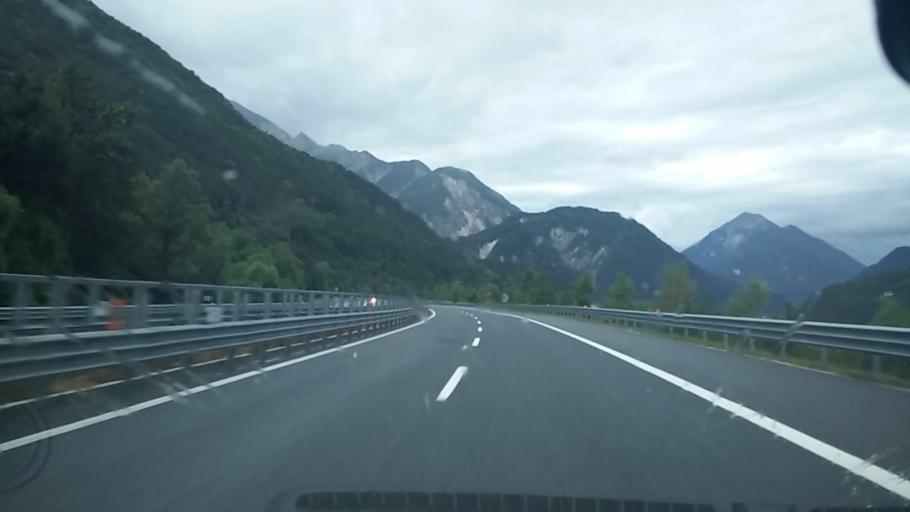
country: IT
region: Friuli Venezia Giulia
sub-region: Provincia di Udine
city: Resiutta
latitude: 46.3947
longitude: 13.2452
